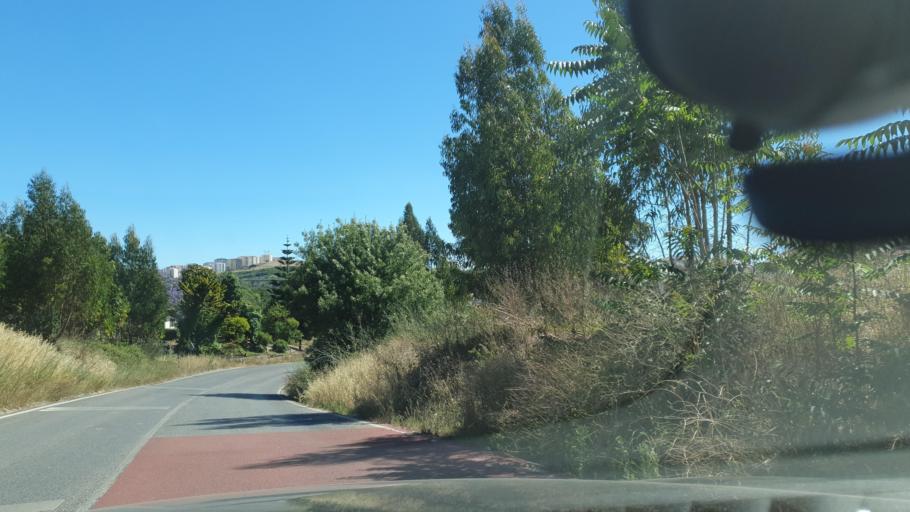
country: PT
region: Lisbon
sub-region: Sintra
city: Belas
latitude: 38.7831
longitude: -9.2592
